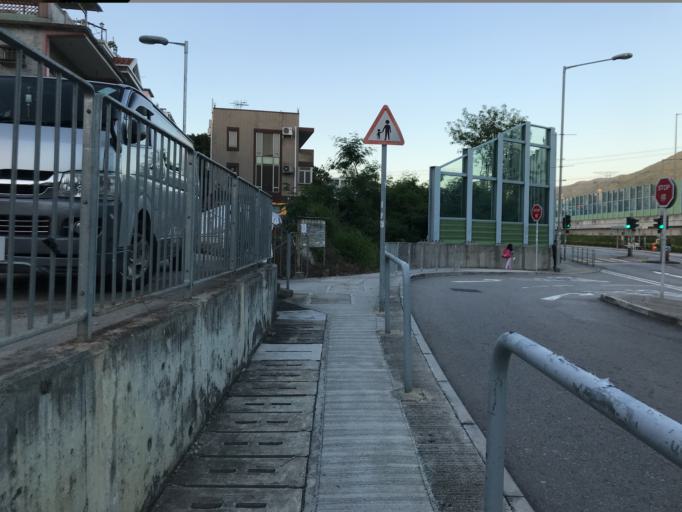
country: HK
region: Tai Po
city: Tai Po
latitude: 22.4633
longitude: 114.1482
